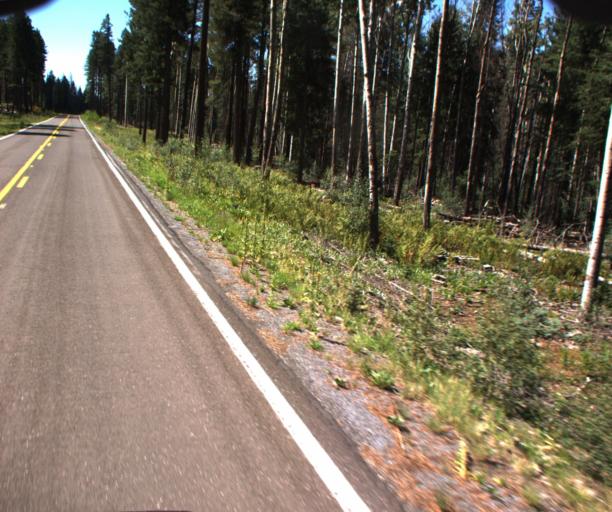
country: US
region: Arizona
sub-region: Apache County
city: Eagar
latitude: 33.6205
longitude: -109.3270
